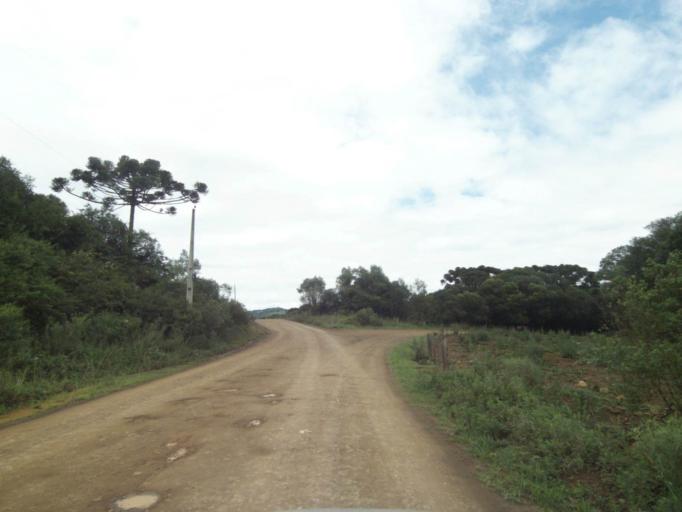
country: BR
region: Rio Grande do Sul
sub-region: Lagoa Vermelha
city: Lagoa Vermelha
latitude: -28.2270
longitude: -51.5389
